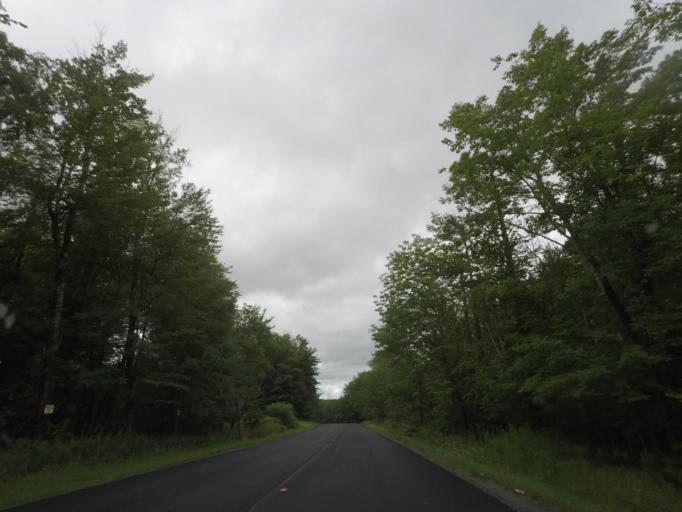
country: US
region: New York
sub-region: Rensselaer County
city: Poestenkill
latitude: 42.6901
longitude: -73.4827
